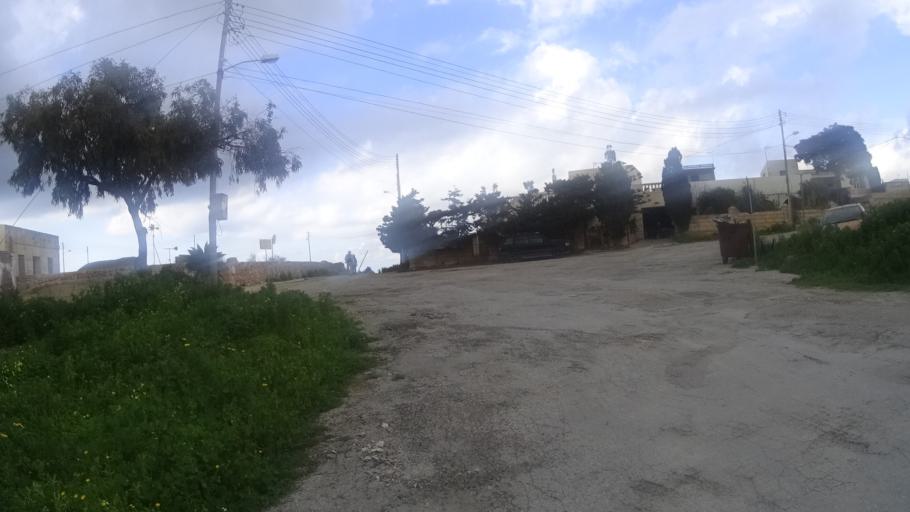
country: MT
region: L-Imgarr
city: Imgarr
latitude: 35.8973
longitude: 14.3656
